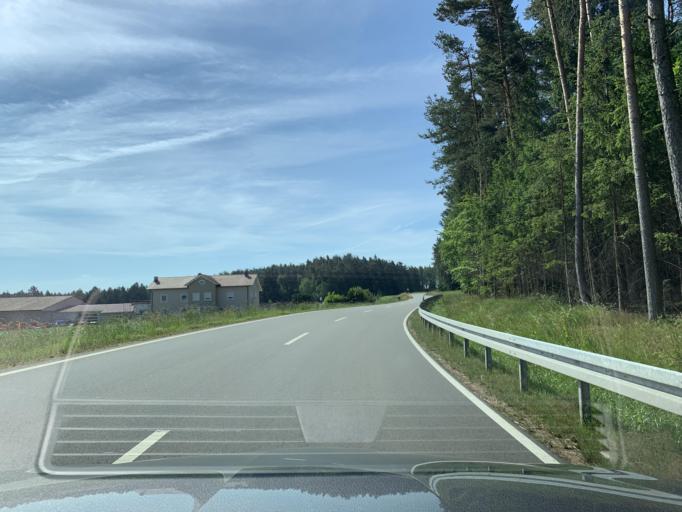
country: DE
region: Bavaria
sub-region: Upper Palatinate
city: Schwarzhofen
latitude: 49.3521
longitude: 12.3253
